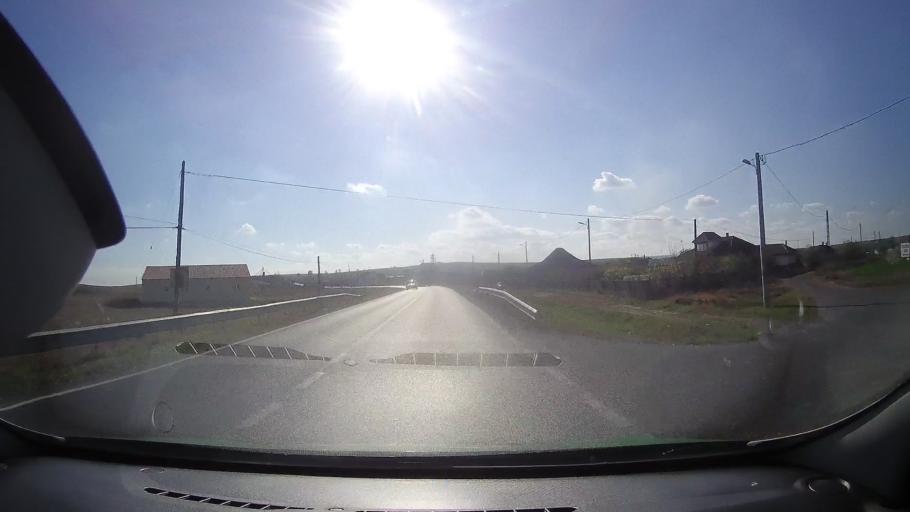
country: RO
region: Tulcea
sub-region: Comuna Baia
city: Baia
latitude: 44.7221
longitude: 28.6794
